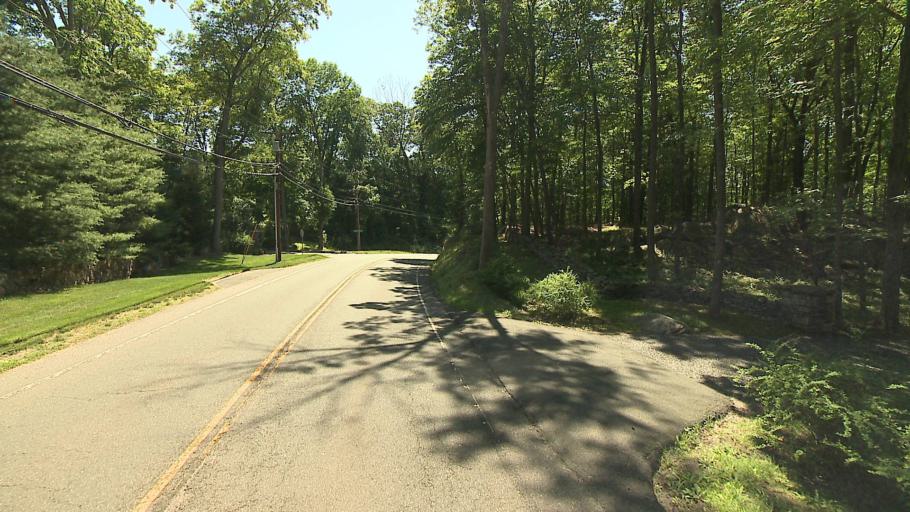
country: US
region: Connecticut
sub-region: Fairfield County
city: Ridgefield
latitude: 41.2946
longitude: -73.5289
